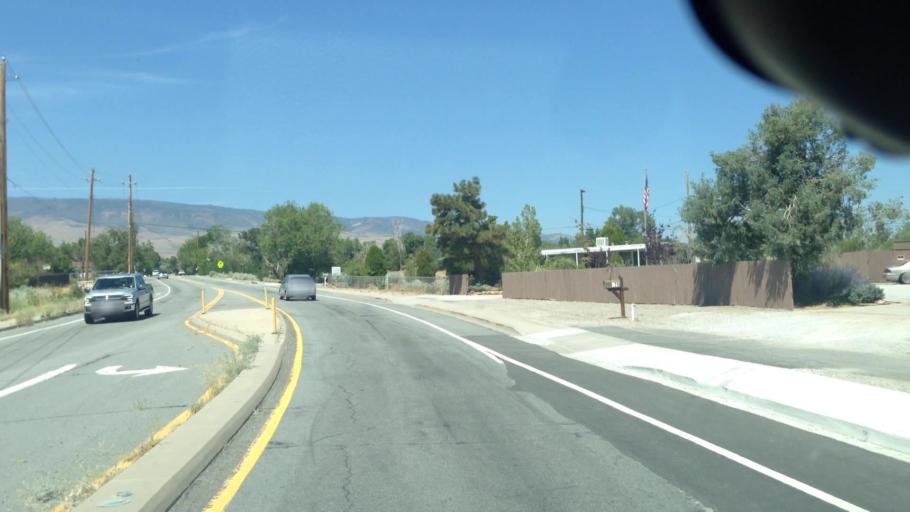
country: US
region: Nevada
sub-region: Washoe County
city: Sparks
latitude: 39.4186
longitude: -119.7606
